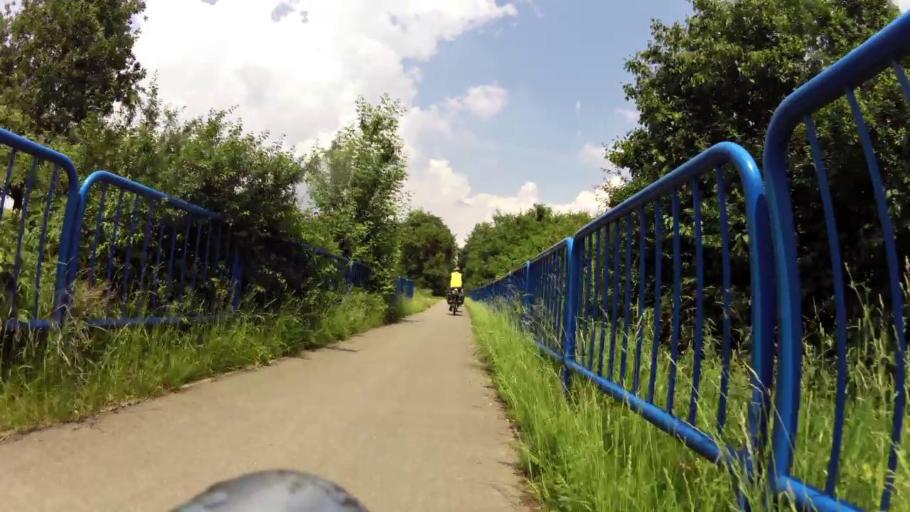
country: PL
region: Kujawsko-Pomorskie
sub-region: Powiat bydgoski
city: Koronowo
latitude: 53.2941
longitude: 17.9478
